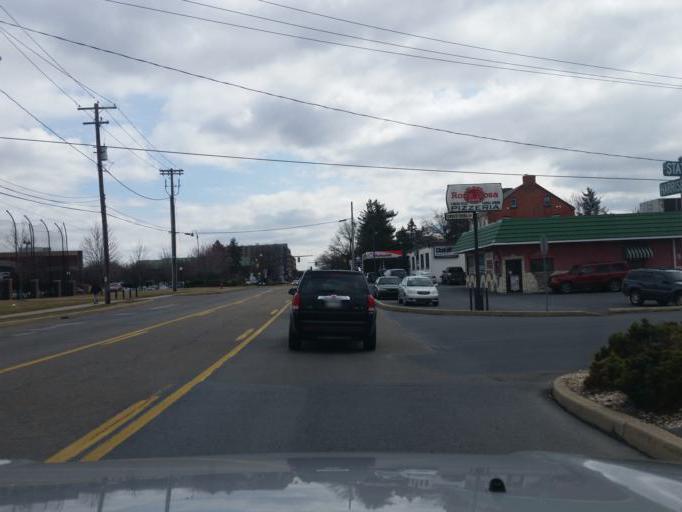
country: US
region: Pennsylvania
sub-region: Lancaster County
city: Lancaster
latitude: 40.0525
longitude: -76.3231
